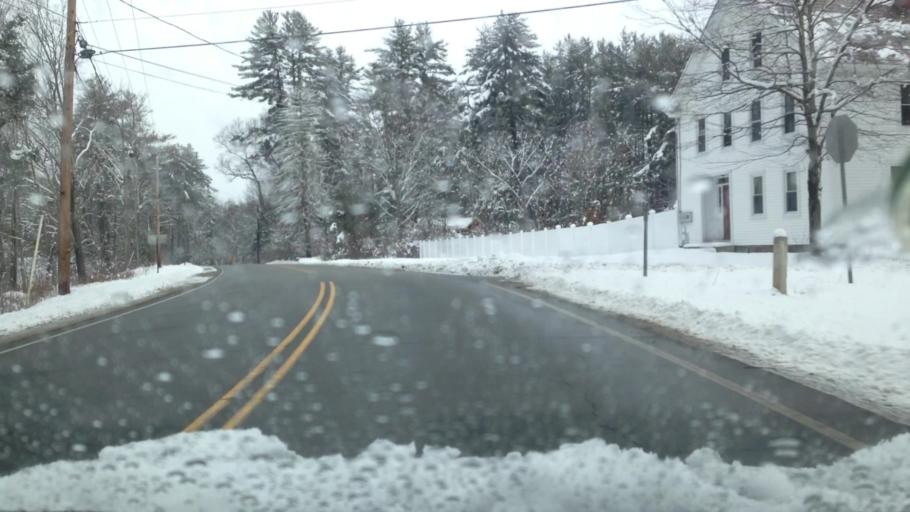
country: US
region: New Hampshire
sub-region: Cheshire County
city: Swanzey
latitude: 42.8444
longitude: -72.2797
